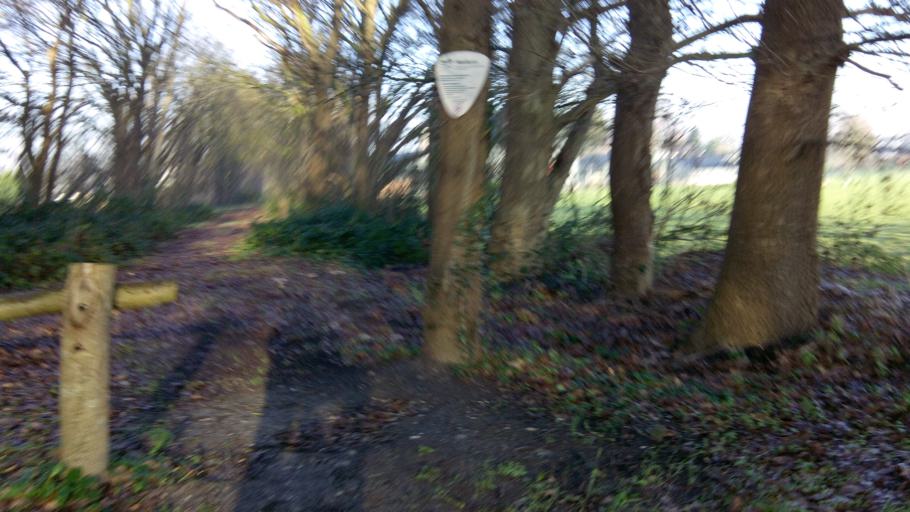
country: NL
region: Utrecht
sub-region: Gemeente Woudenberg
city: Woudenberg
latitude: 52.0774
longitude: 5.4529
